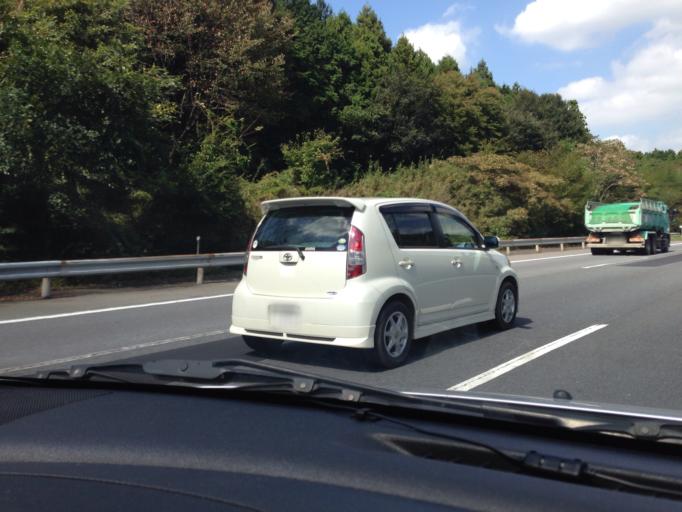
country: JP
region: Ibaraki
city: Naka
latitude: 36.0820
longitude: 140.1547
